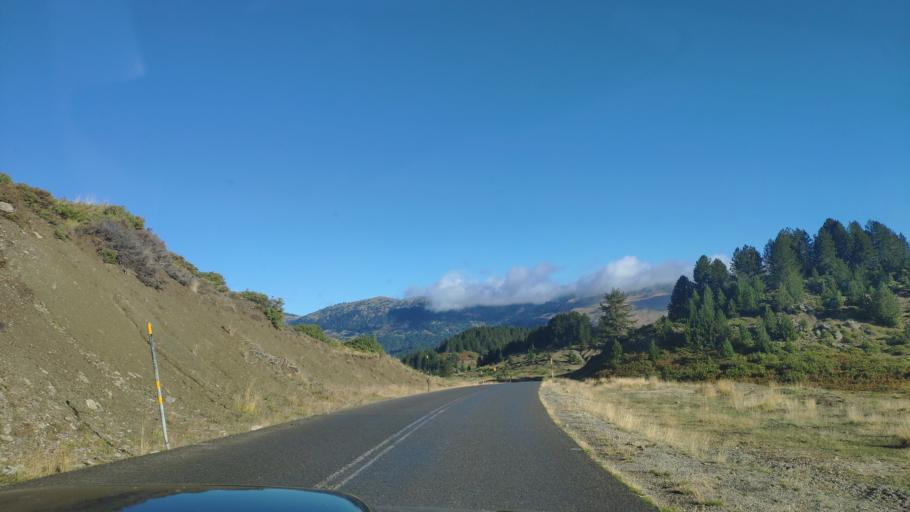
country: GR
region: Epirus
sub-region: Nomos Ioanninon
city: Metsovo
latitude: 39.8011
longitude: 21.1748
